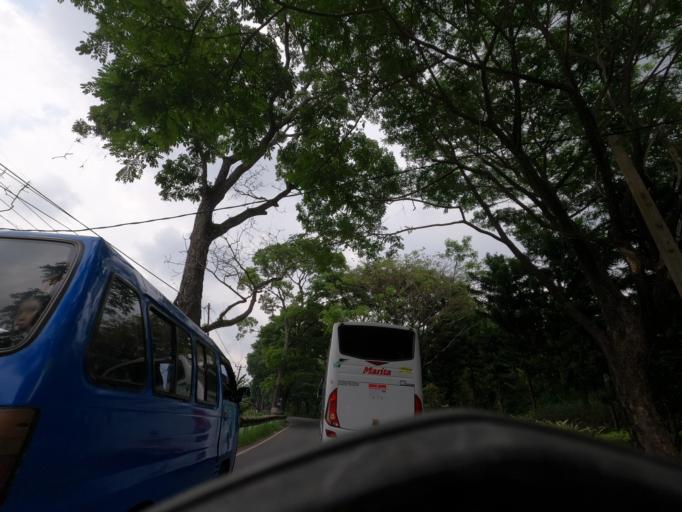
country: ID
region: West Java
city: Ciranjang-hilir
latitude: -6.7909
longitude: 107.0703
